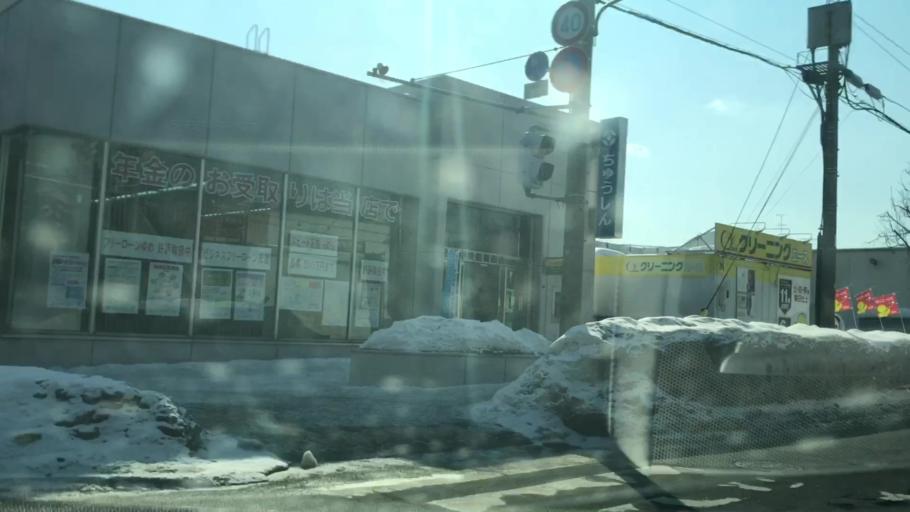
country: JP
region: Hokkaido
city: Sapporo
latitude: 43.0236
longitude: 141.3918
